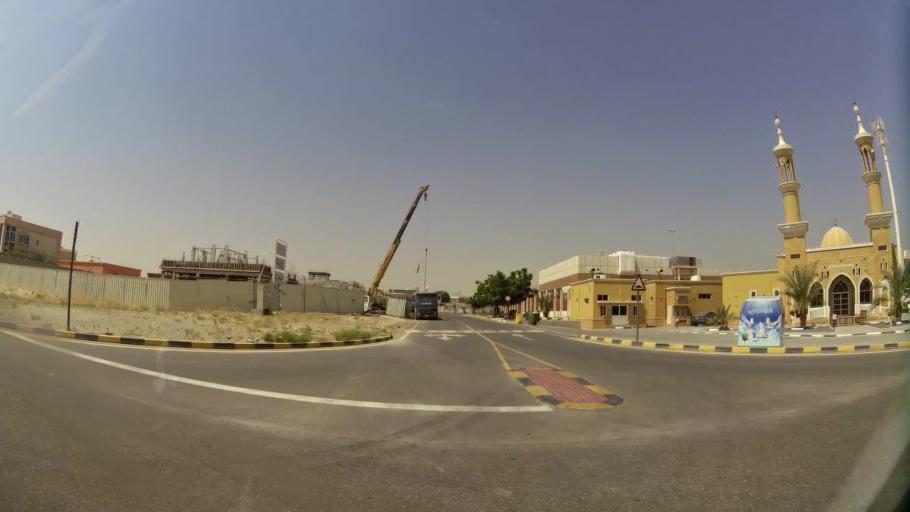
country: AE
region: Ajman
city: Ajman
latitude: 25.4205
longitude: 55.5190
